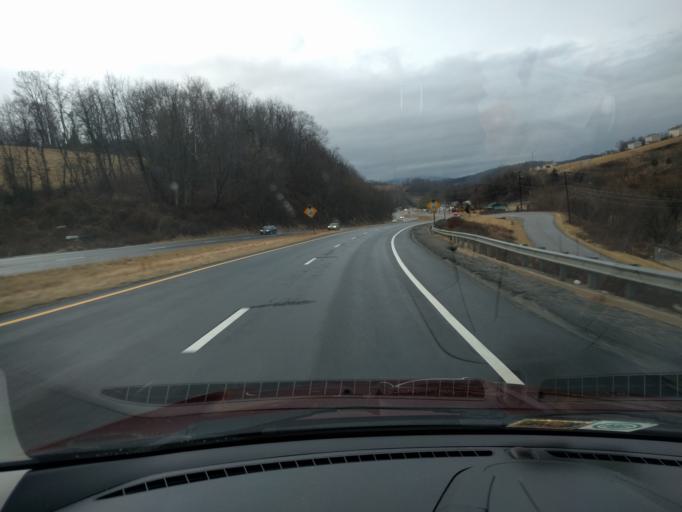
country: US
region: Virginia
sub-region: Giles County
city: Pembroke
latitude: 37.3194
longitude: -80.6109
